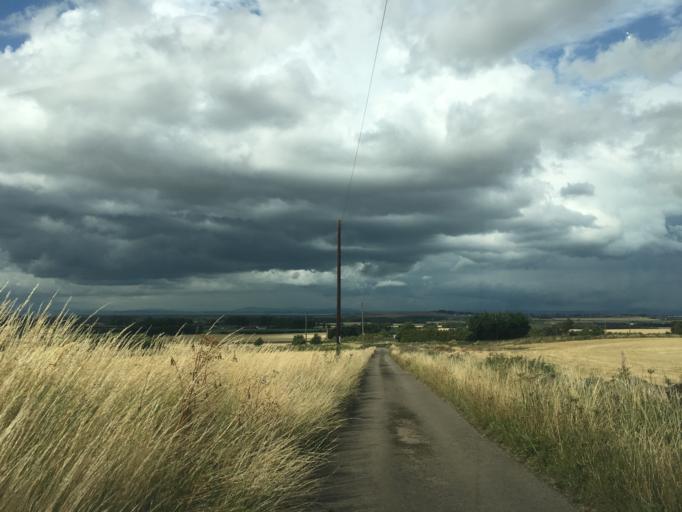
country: GB
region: Scotland
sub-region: East Lothian
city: Haddington
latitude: 55.9940
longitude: -2.7957
